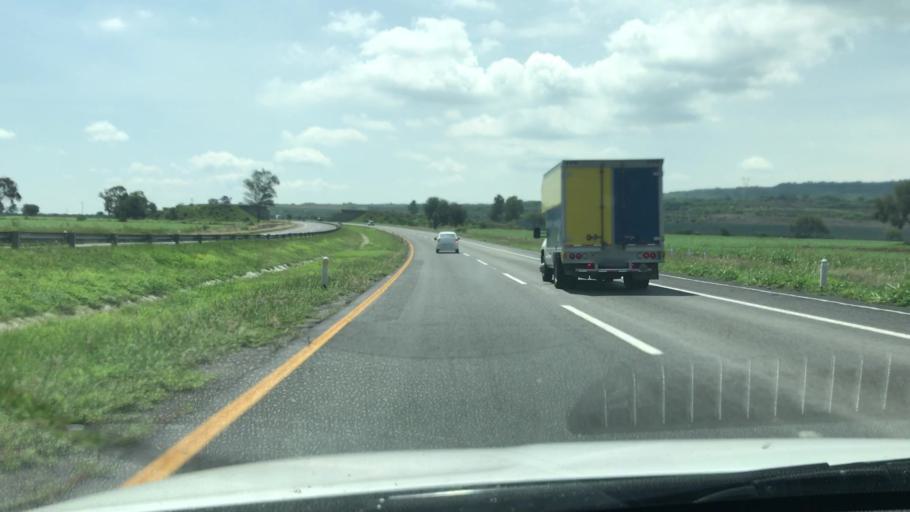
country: MX
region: Jalisco
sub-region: Poncitlan
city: Santa Cruz el Grande
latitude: 20.4429
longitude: -102.8611
